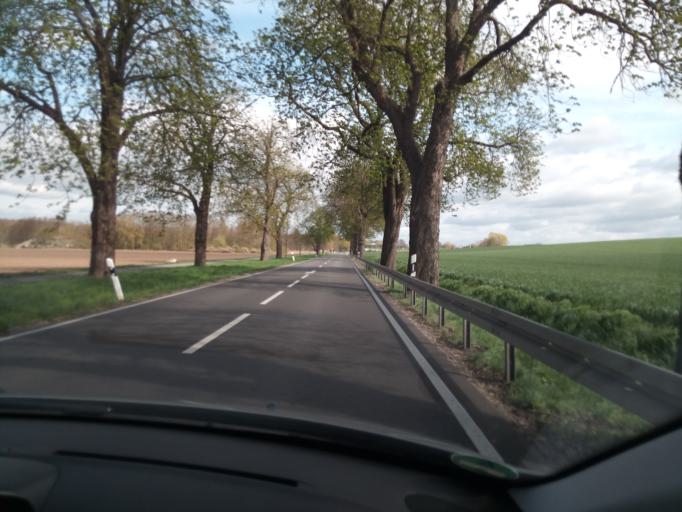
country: DE
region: Mecklenburg-Vorpommern
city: Boizenburg
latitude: 53.4185
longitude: 10.7445
